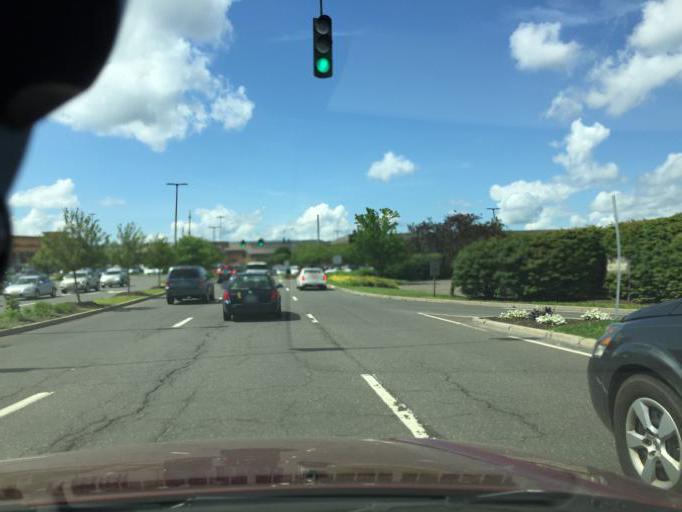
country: US
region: Connecticut
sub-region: Fairfield County
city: Danbury
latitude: 41.3783
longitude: -73.4778
